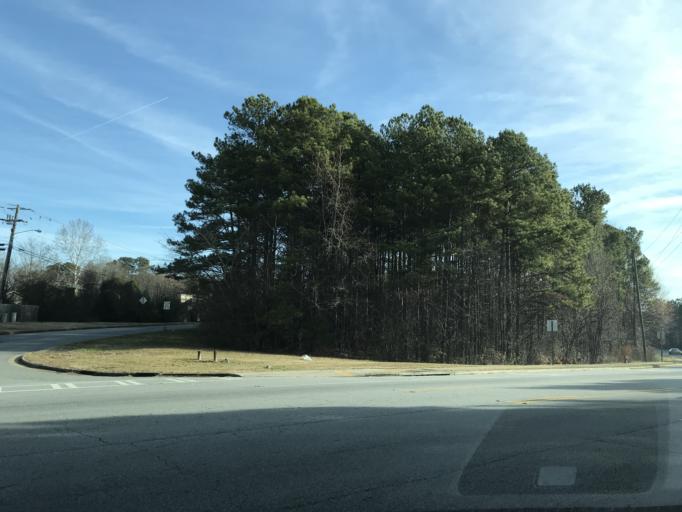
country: US
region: Georgia
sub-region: Cobb County
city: Kennesaw
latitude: 34.0605
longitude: -84.5969
